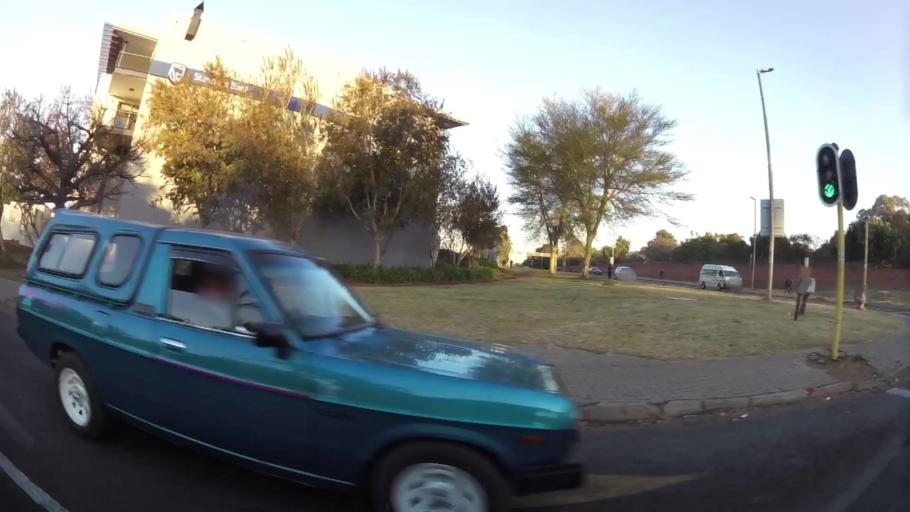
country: ZA
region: North-West
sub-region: Bojanala Platinum District Municipality
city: Rustenburg
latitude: -25.6761
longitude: 27.2465
